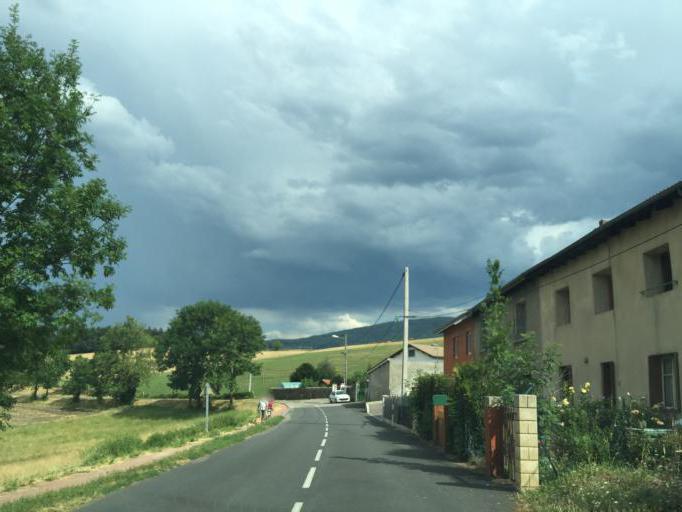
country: FR
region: Rhone-Alpes
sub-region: Departement de la Loire
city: Saint-Jean-Bonnefonds
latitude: 45.4466
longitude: 4.4524
